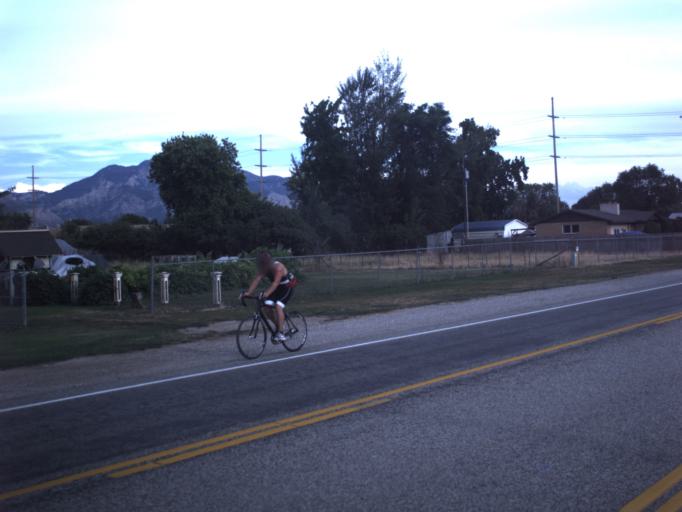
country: US
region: Utah
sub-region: Weber County
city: Farr West
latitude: 41.2995
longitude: -112.0278
